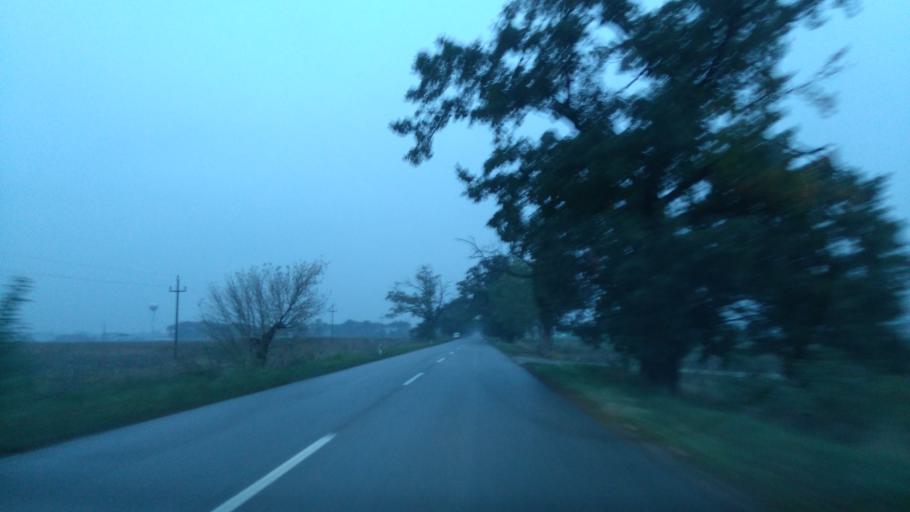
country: RS
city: Backo Petrovo Selo
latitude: 45.6847
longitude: 20.0719
